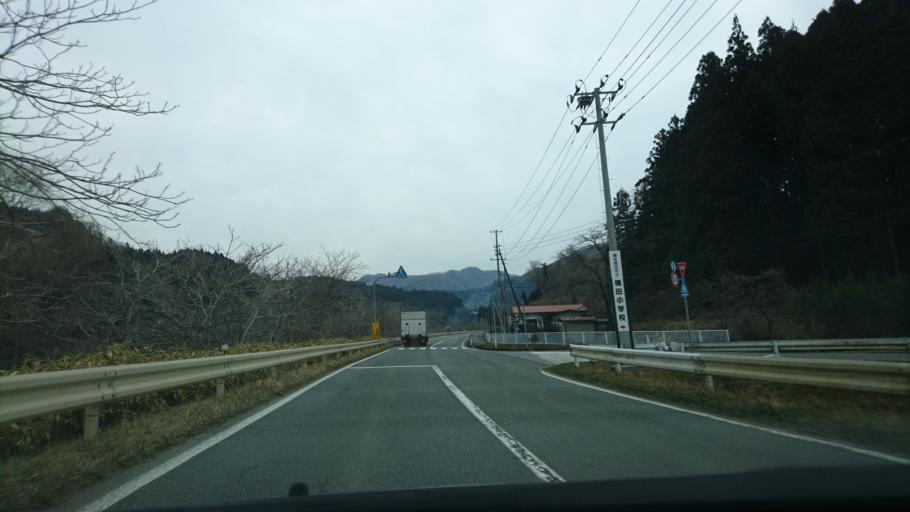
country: JP
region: Iwate
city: Ofunato
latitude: 39.0855
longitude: 141.5805
